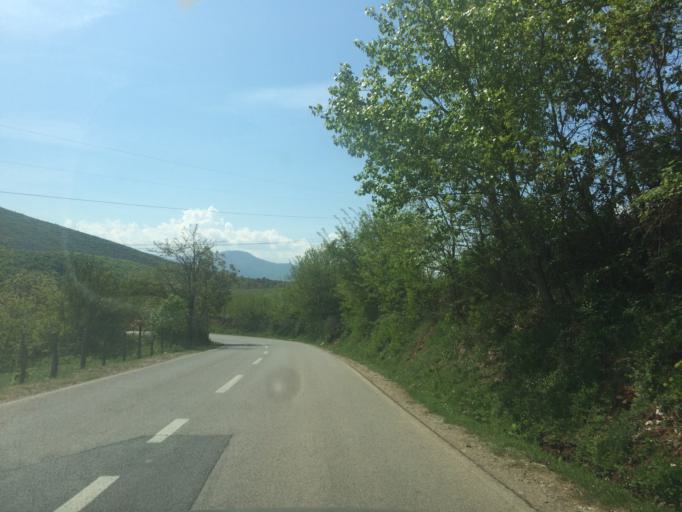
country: AL
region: Kukes
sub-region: Rrethi i Tropojes
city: Llugaj
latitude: 42.3798
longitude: 20.1302
